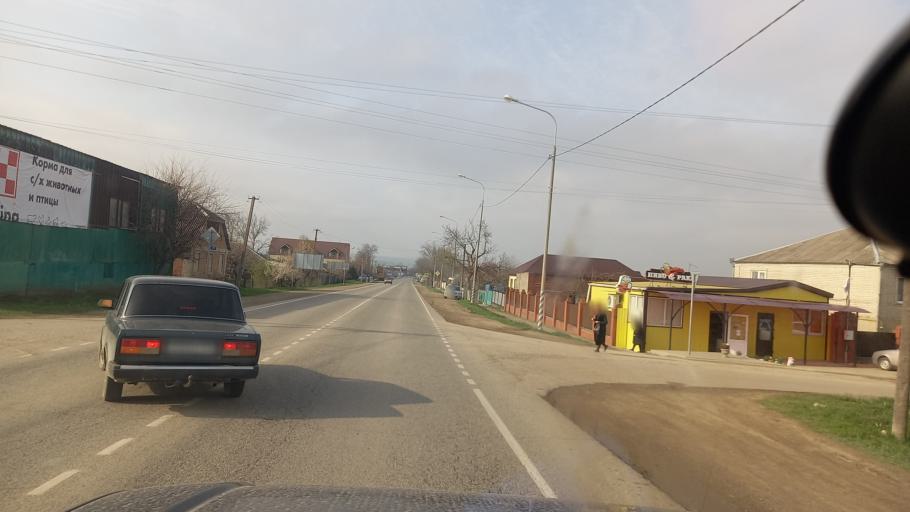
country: RU
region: Krasnodarskiy
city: Varenikovskaya
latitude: 45.1150
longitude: 37.6191
